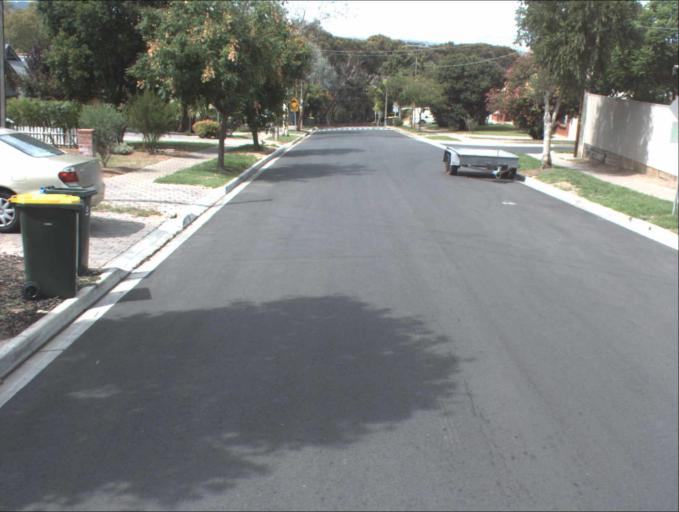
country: AU
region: South Australia
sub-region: Campbelltown
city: Paradise
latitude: -34.8601
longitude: 138.6673
